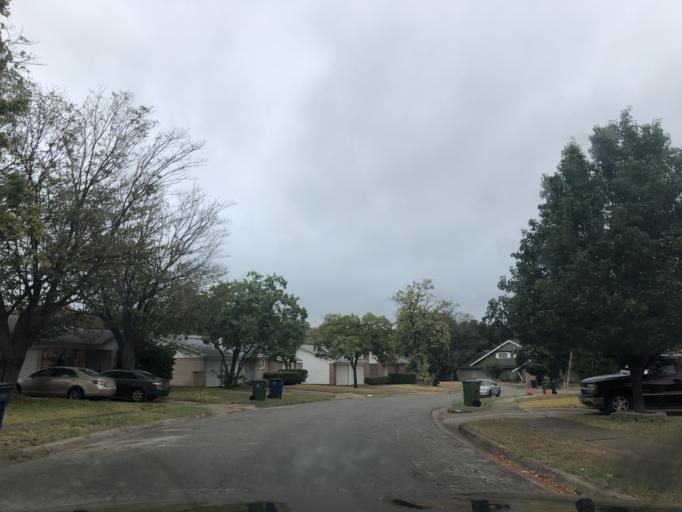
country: US
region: Texas
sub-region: Dallas County
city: Garland
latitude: 32.8728
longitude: -96.6450
